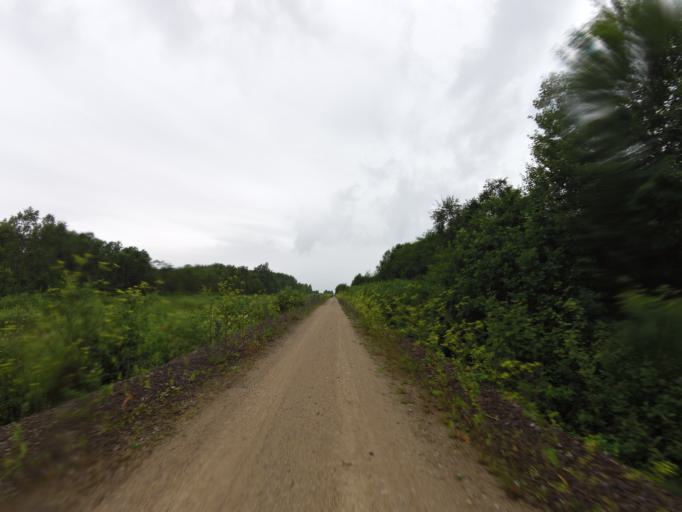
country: EE
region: Laeaene
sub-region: Ridala Parish
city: Uuemoisa
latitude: 58.9550
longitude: 23.8302
